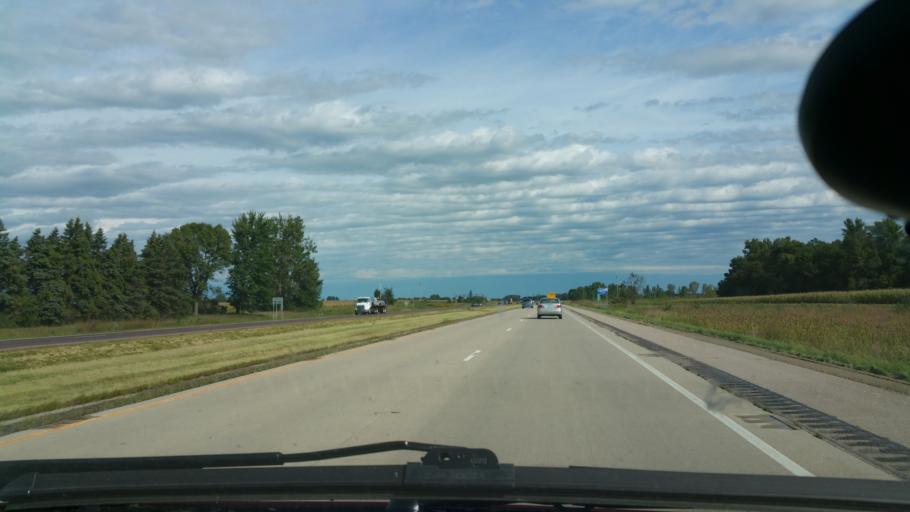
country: US
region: Minnesota
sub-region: Steele County
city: Owatonna
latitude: 43.9176
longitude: -93.2769
